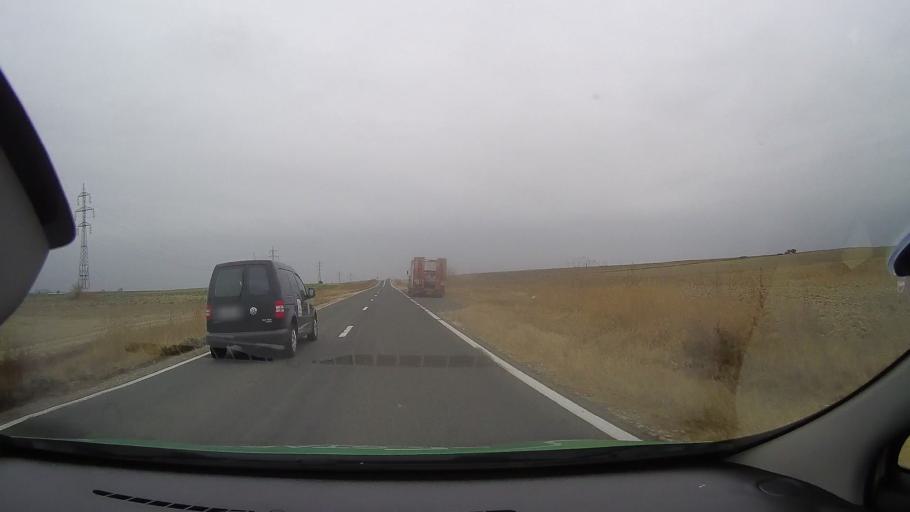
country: RO
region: Constanta
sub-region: Comuna Ciobanu
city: Ciobanu
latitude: 44.6953
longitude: 27.9850
